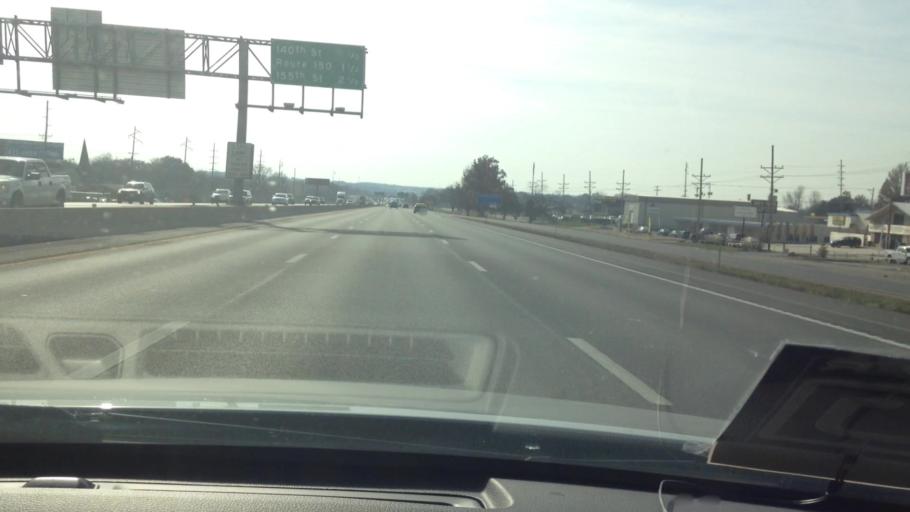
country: US
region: Missouri
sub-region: Jackson County
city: Grandview
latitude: 38.8825
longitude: -94.5257
